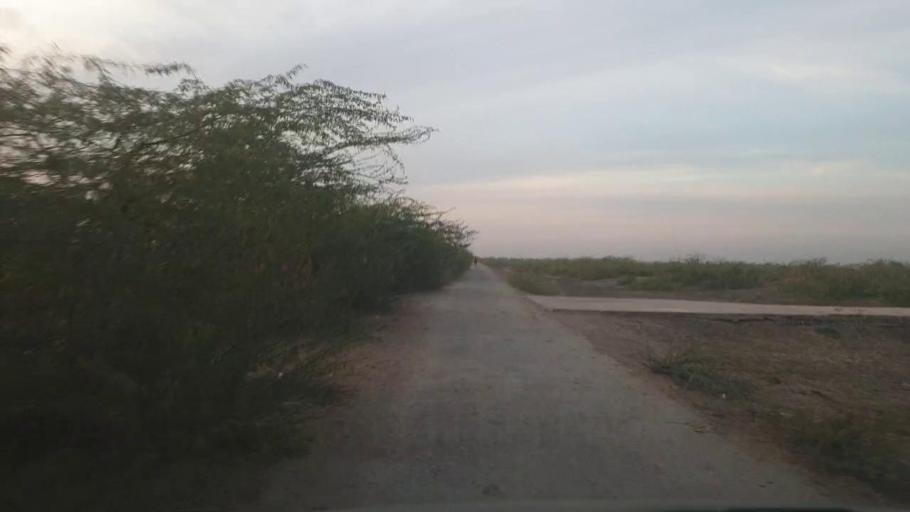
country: PK
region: Sindh
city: Kunri
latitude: 25.2289
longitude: 69.5337
